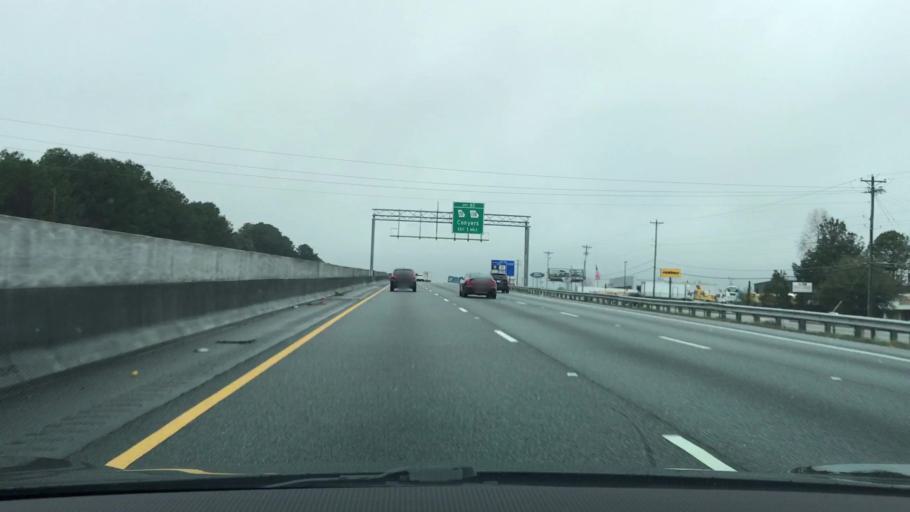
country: US
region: Georgia
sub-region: Rockdale County
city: Conyers
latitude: 33.6431
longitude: -83.9888
